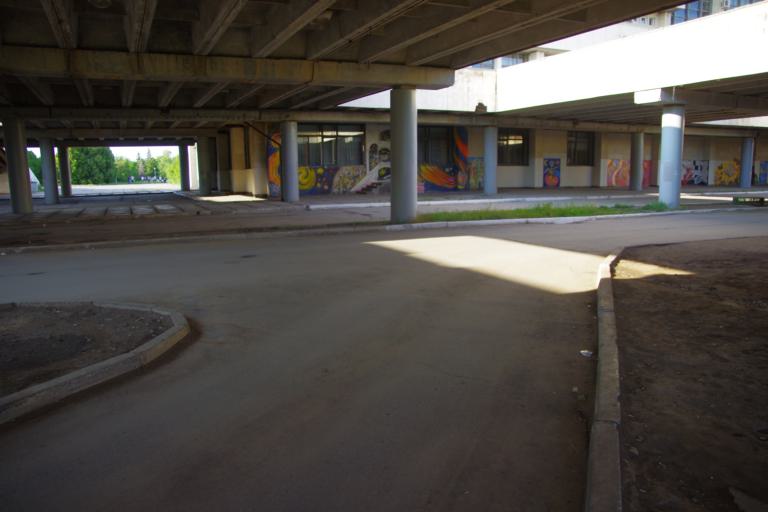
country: RU
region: Samara
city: Tol'yatti
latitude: 53.5175
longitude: 49.2747
